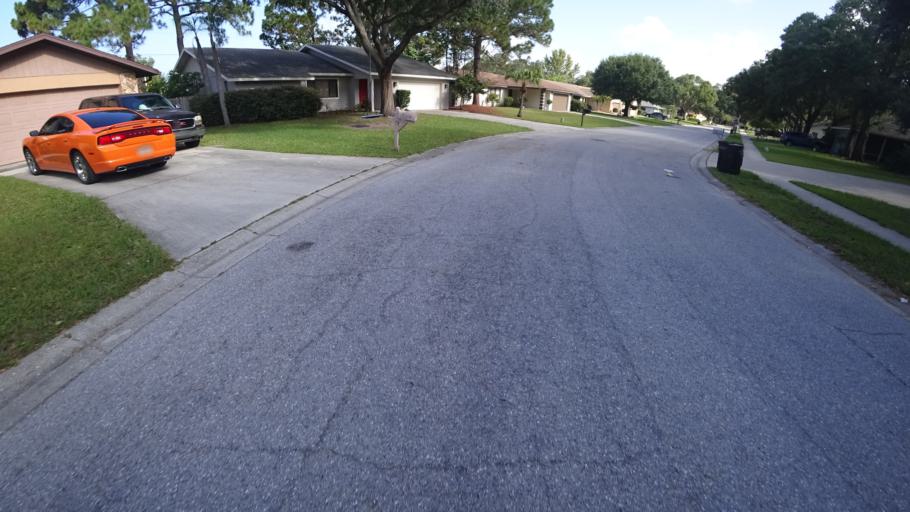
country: US
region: Florida
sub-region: Sarasota County
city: Desoto Lakes
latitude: 27.3893
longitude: -82.5011
